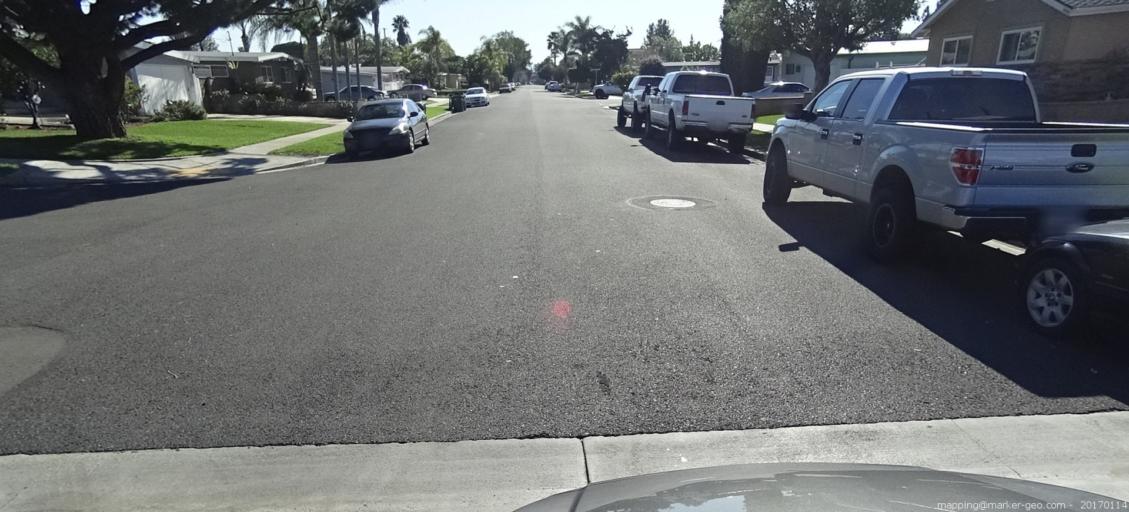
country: US
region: California
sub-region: Orange County
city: Tustin
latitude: 33.7550
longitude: -117.8180
